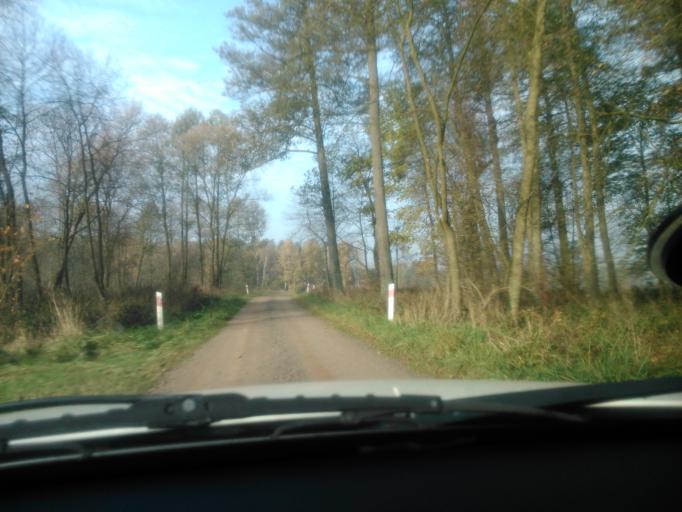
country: PL
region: Kujawsko-Pomorskie
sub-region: Powiat golubsko-dobrzynski
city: Radomin
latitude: 53.1609
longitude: 19.1455
